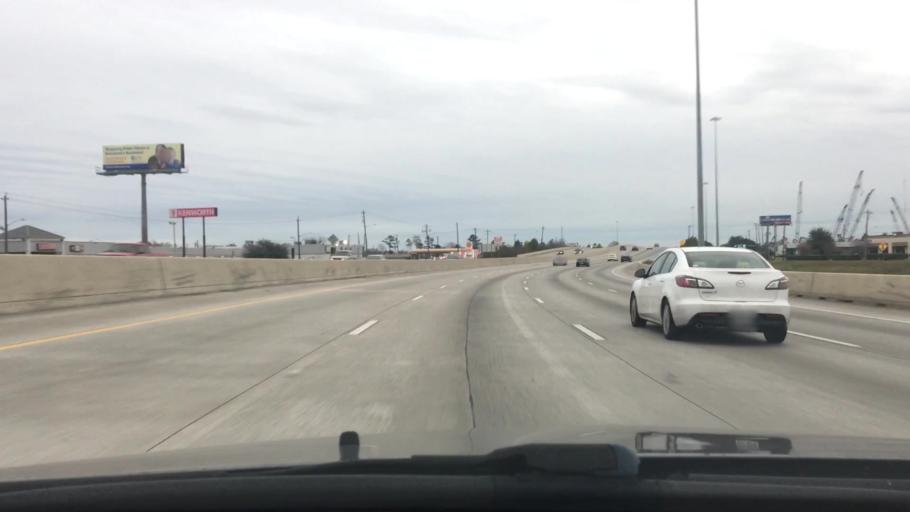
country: US
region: Texas
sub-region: Harris County
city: Houston
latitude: 29.8091
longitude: -95.3056
